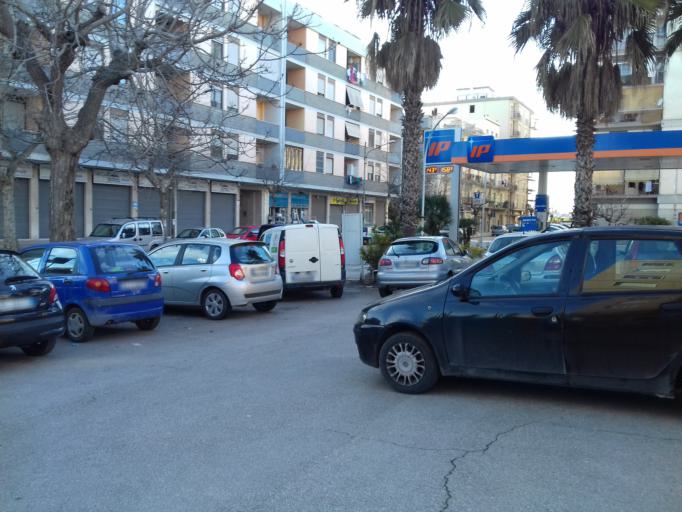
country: IT
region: Apulia
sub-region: Provincia di Bari
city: Ruvo di Puglia
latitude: 41.1145
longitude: 16.4810
